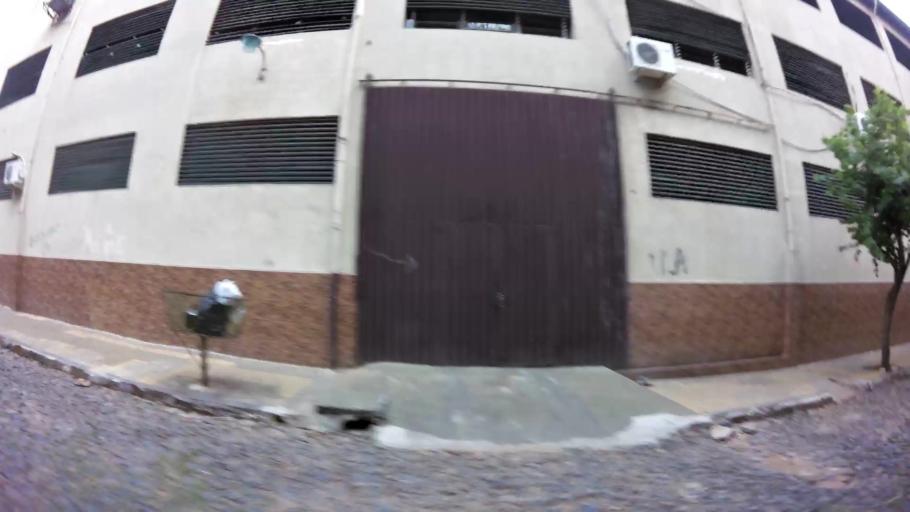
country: PY
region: Asuncion
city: Asuncion
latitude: -25.3122
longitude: -57.6073
